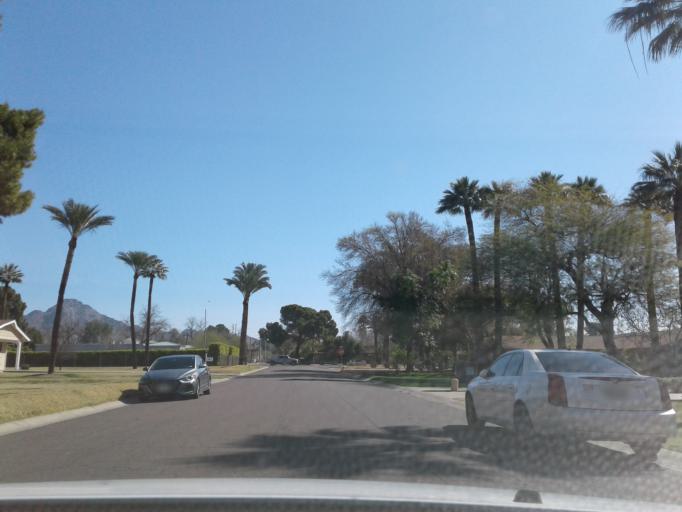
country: US
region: Arizona
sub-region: Maricopa County
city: Phoenix
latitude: 33.5346
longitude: -112.0665
